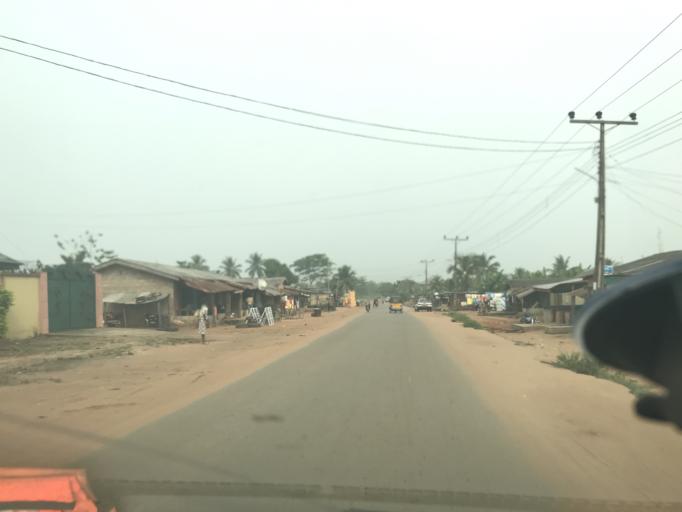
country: NG
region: Ogun
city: Ado Odo
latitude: 6.5000
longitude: 2.9544
